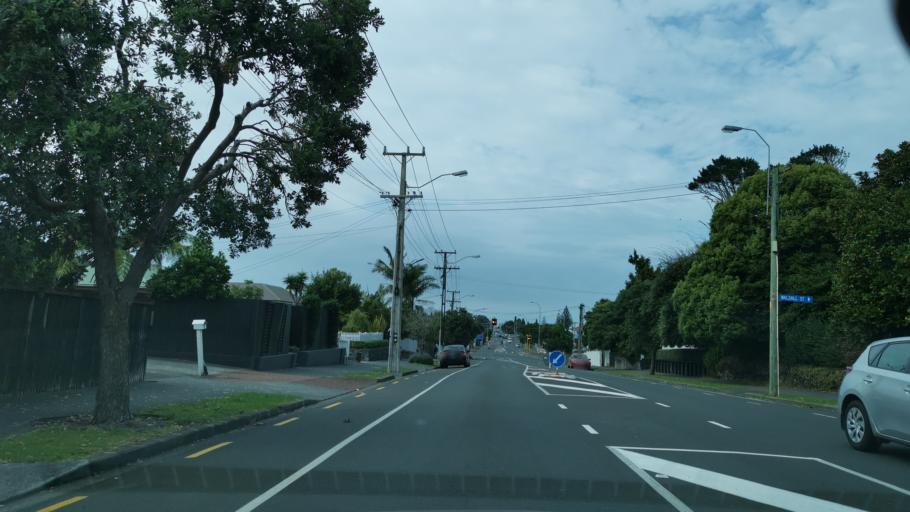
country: NZ
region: Auckland
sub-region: Auckland
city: Rosebank
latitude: -36.8928
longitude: 174.7008
